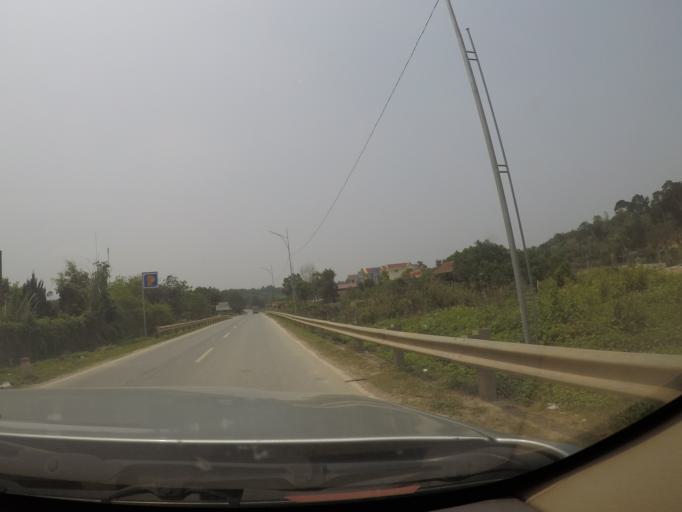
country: VN
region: Thanh Hoa
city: Thi Tran Yen Cat
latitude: 19.6698
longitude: 105.4446
